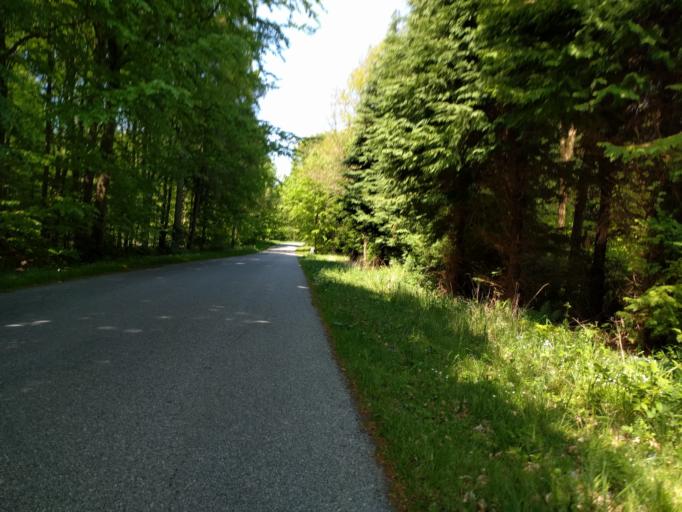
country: DK
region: Zealand
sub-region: Guldborgsund Kommune
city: Stubbekobing
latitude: 54.8356
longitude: 12.1344
